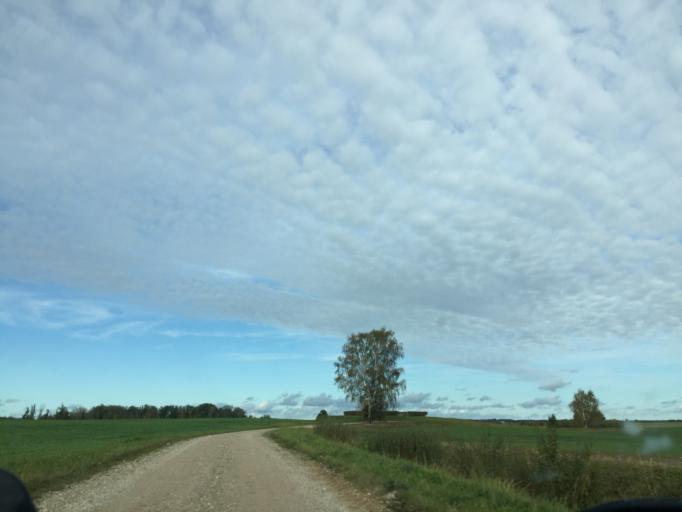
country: LV
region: Jaunpils
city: Jaunpils
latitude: 56.6513
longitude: 23.0771
